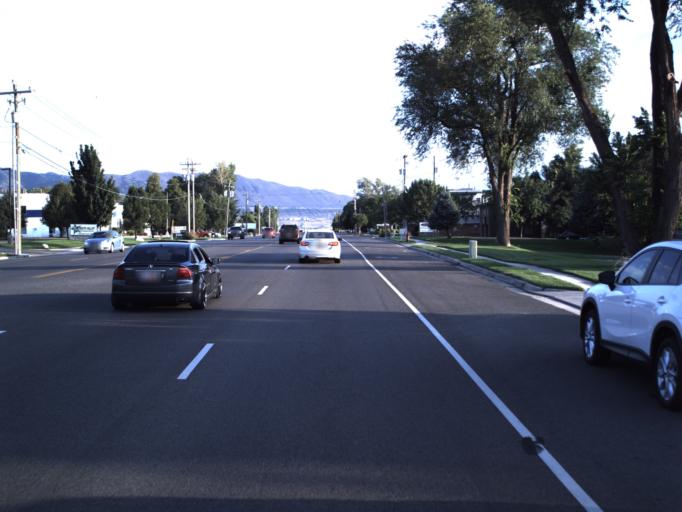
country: US
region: Utah
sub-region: Salt Lake County
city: Draper
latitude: 40.5428
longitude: -111.8914
